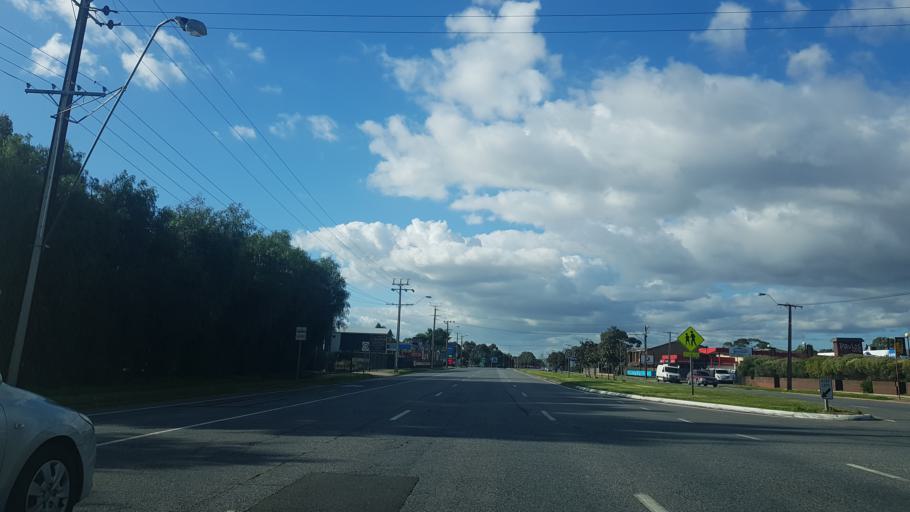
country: AU
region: South Australia
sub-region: Salisbury
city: Ingle Farm
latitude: -34.8286
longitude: 138.6142
